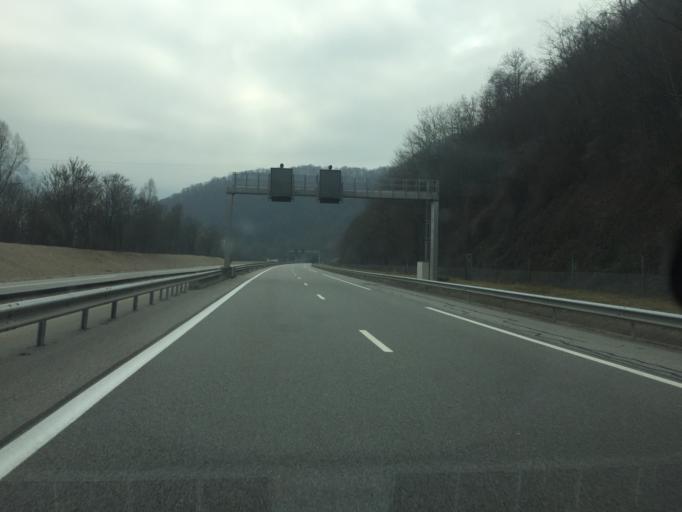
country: FR
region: Rhone-Alpes
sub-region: Departement de la Savoie
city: Aiton
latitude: 45.5240
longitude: 6.3088
